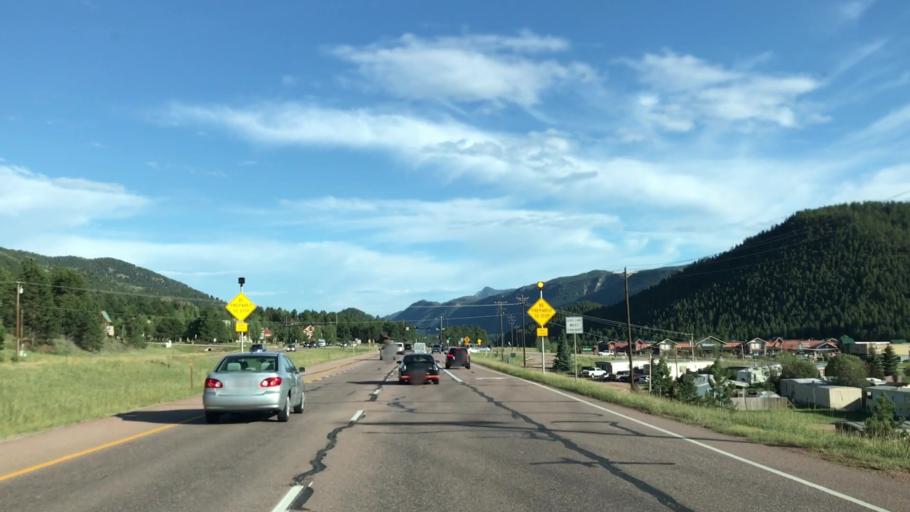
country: US
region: Colorado
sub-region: Teller County
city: Woodland Park
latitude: 38.9763
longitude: -105.0401
